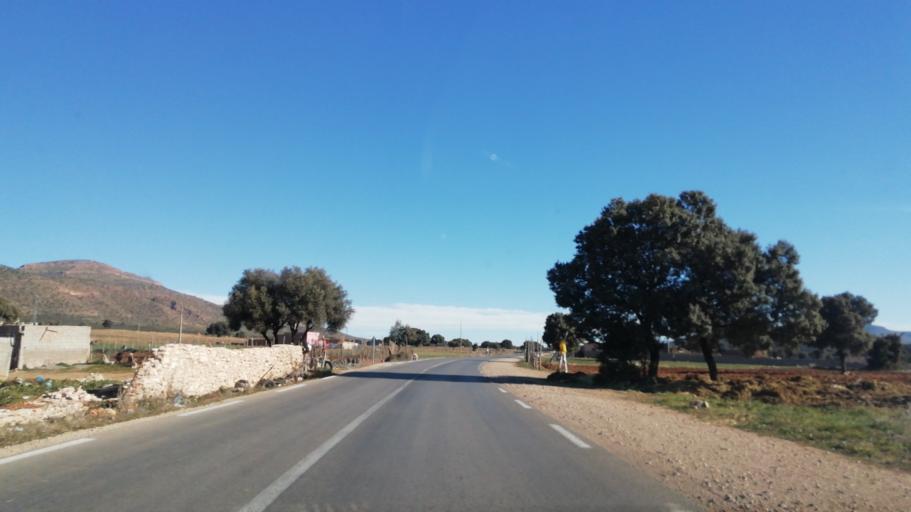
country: DZ
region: Tlemcen
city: Sebdou
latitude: 34.6961
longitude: -1.2358
